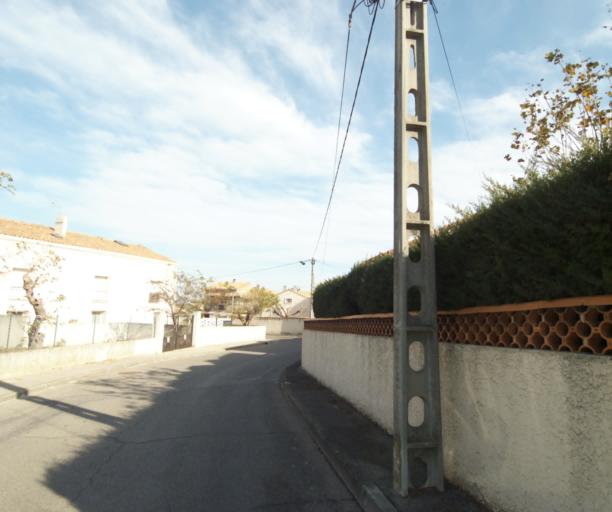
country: FR
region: Provence-Alpes-Cote d'Azur
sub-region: Departement des Bouches-du-Rhone
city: Chateauneuf-les-Martigues
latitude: 43.3829
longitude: 5.1686
